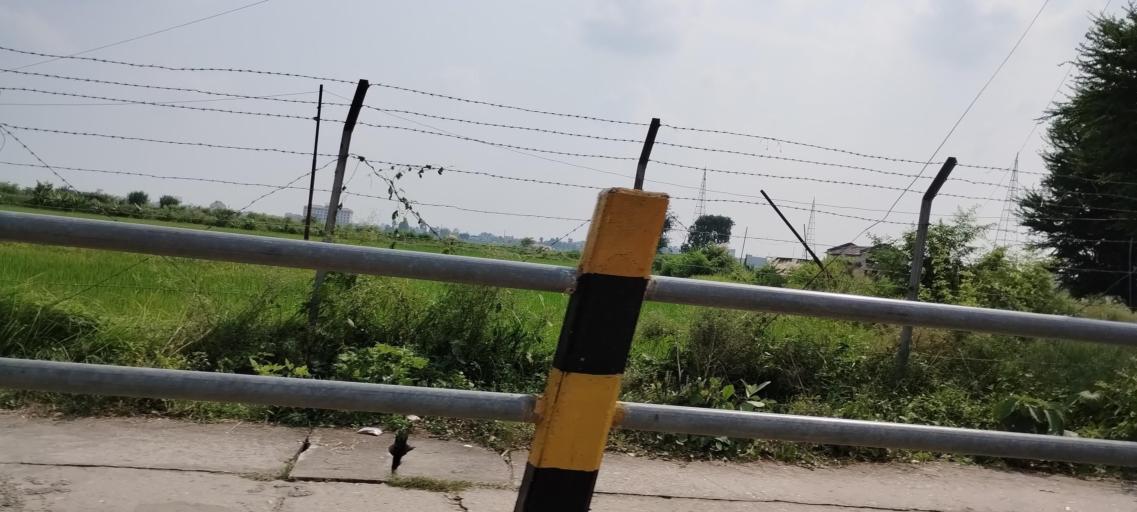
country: NP
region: Mid Western
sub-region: Bheri Zone
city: Nepalgunj
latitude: 28.0989
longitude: 81.6592
